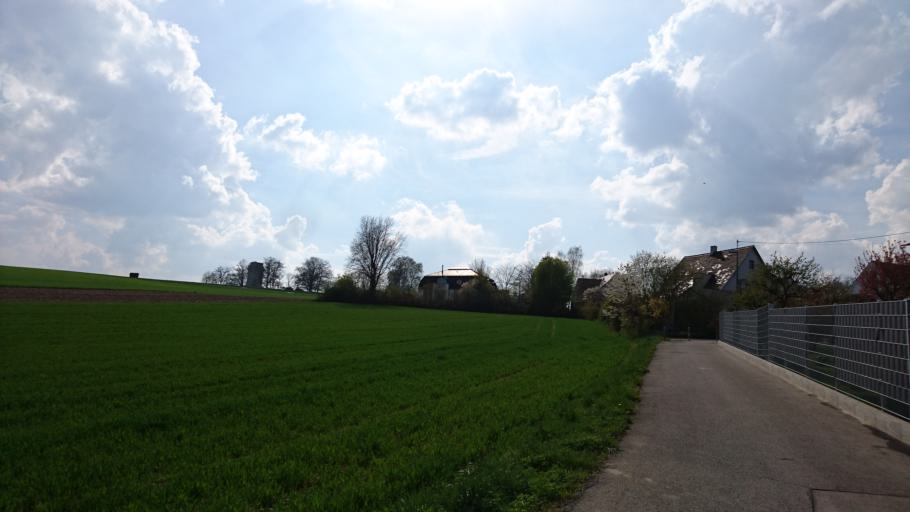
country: DE
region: Bavaria
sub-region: Swabia
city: Stadtbergen
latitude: 48.3748
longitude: 10.8334
